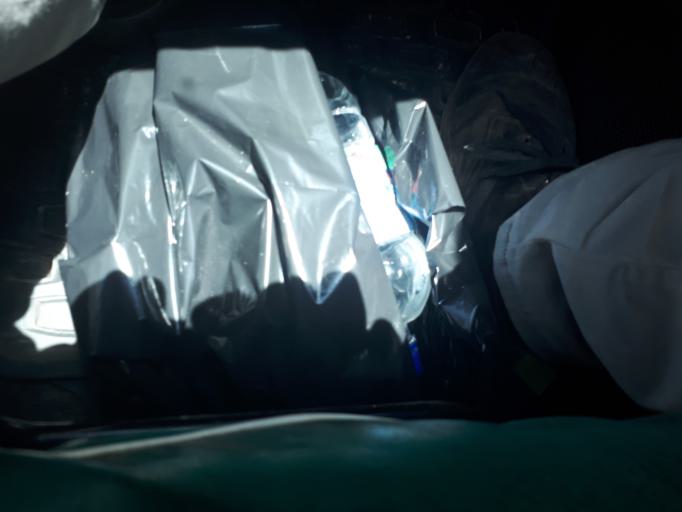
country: VU
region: Sanma
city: Luganville
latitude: -15.5782
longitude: 167.1224
